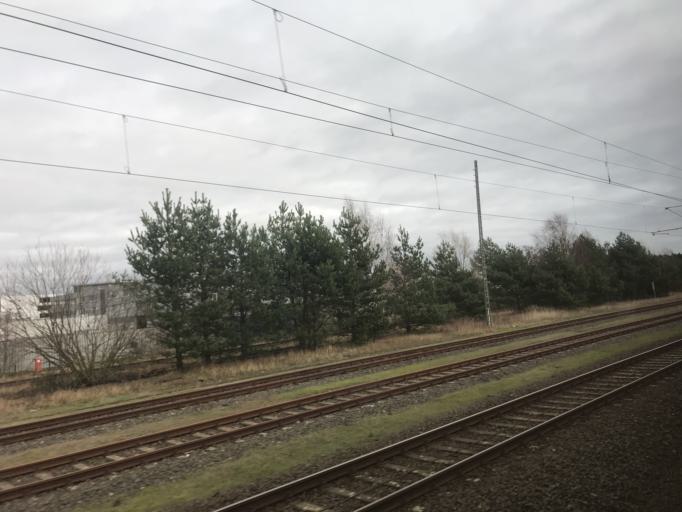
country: DE
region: Lower Saxony
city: Gifhorn
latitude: 52.4551
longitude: 10.5515
